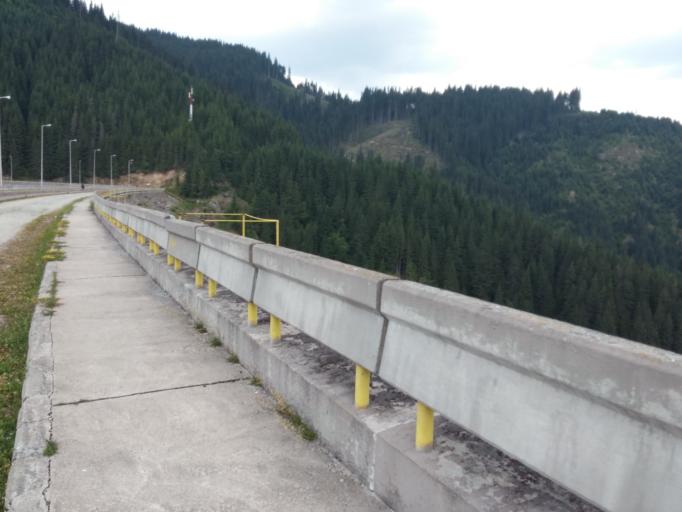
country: RO
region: Valcea
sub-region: Comuna Voineasa
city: Voineasa
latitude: 45.4465
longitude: 23.7691
